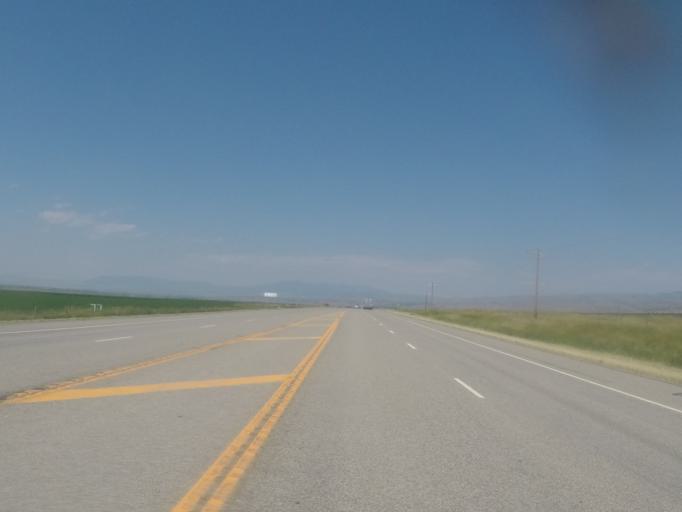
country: US
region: Montana
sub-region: Broadwater County
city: Townsend
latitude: 46.1096
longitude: -111.5085
